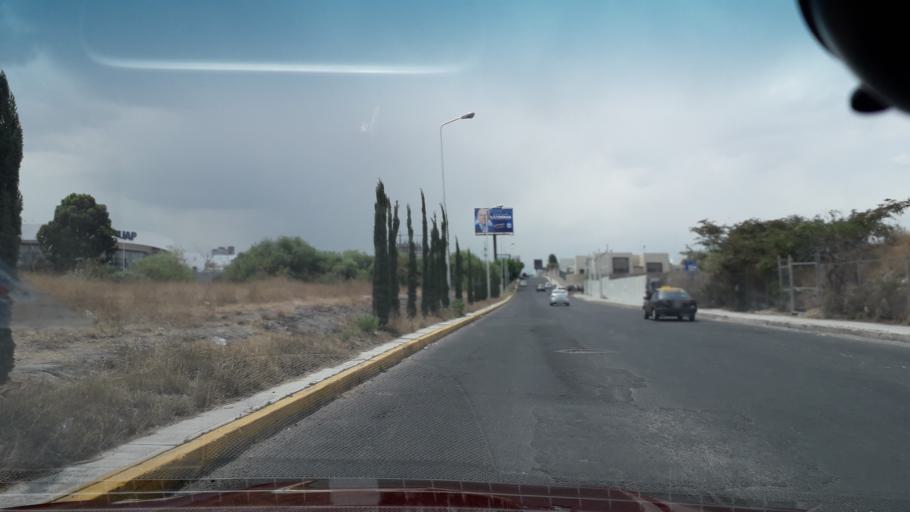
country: MX
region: Puebla
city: Puebla
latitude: 19.0199
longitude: -98.2361
